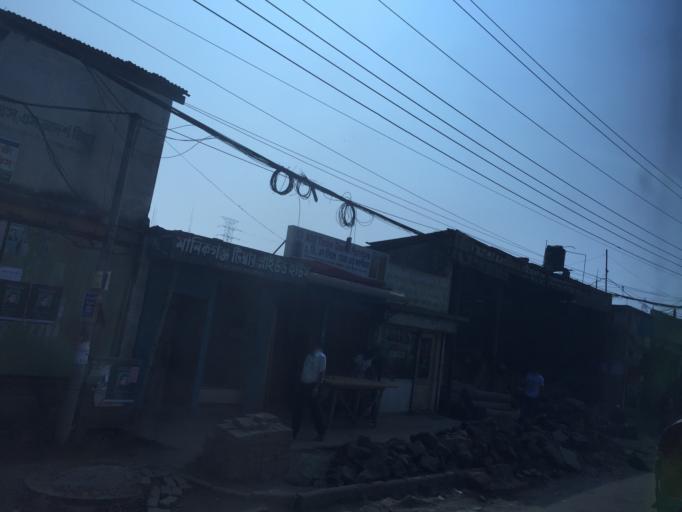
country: BD
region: Dhaka
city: Paltan
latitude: 23.7711
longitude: 90.4251
